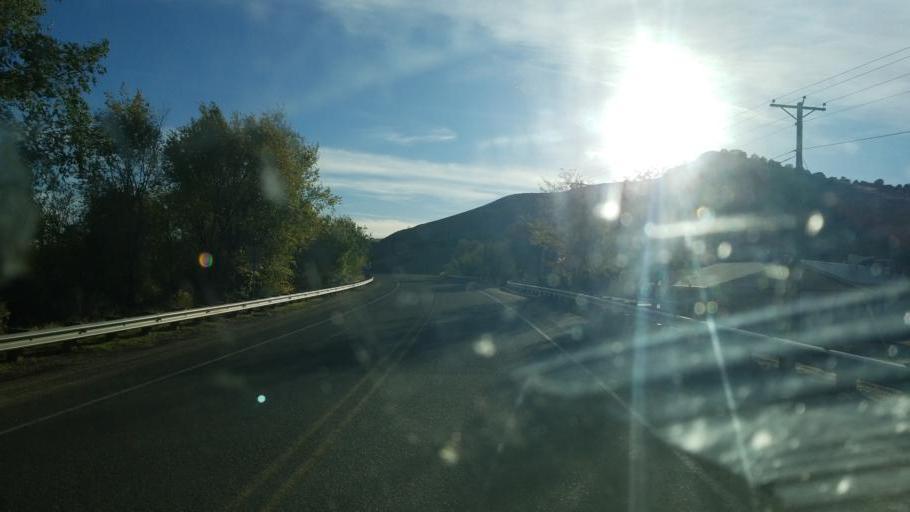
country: US
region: New Mexico
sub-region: San Juan County
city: Bloomfield
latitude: 36.7216
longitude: -107.8320
